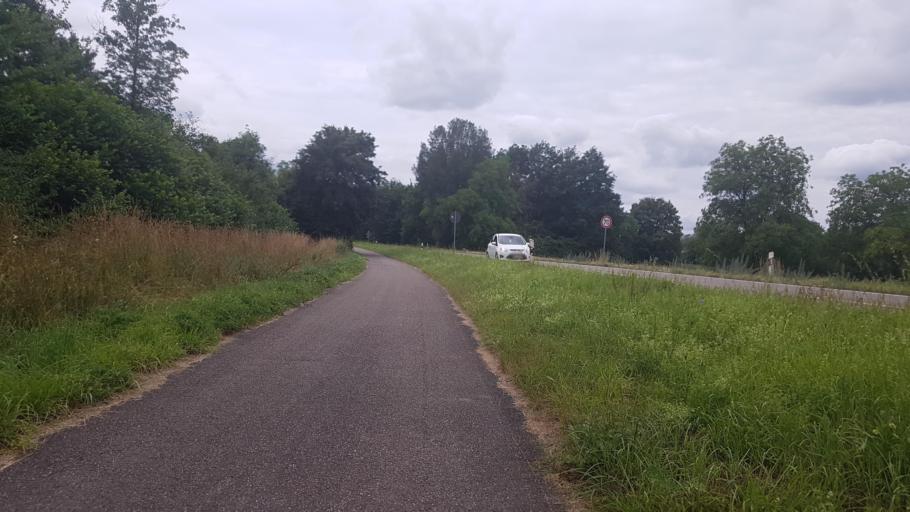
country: DE
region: Baden-Wuerttemberg
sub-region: Karlsruhe Region
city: Steinmauern
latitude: 48.8847
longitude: 8.2071
